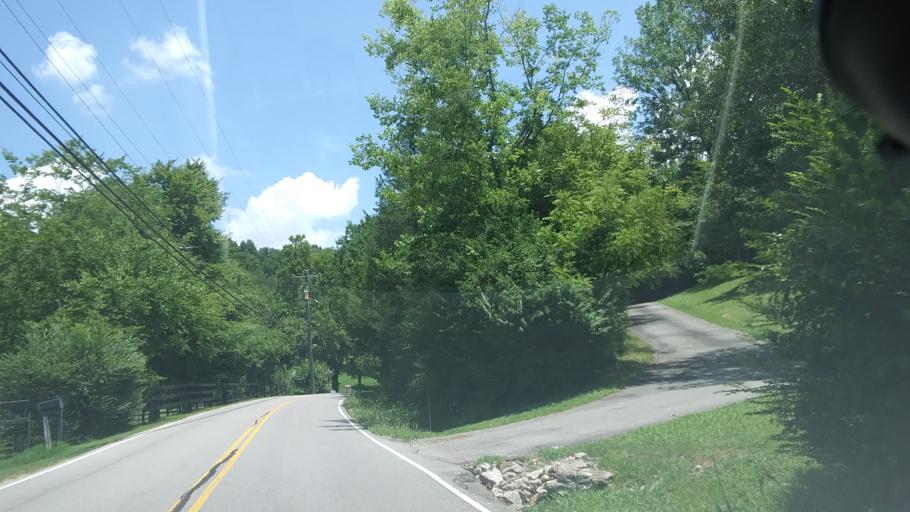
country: US
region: Tennessee
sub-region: Davidson County
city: Belle Meade
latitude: 36.1216
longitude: -86.9321
